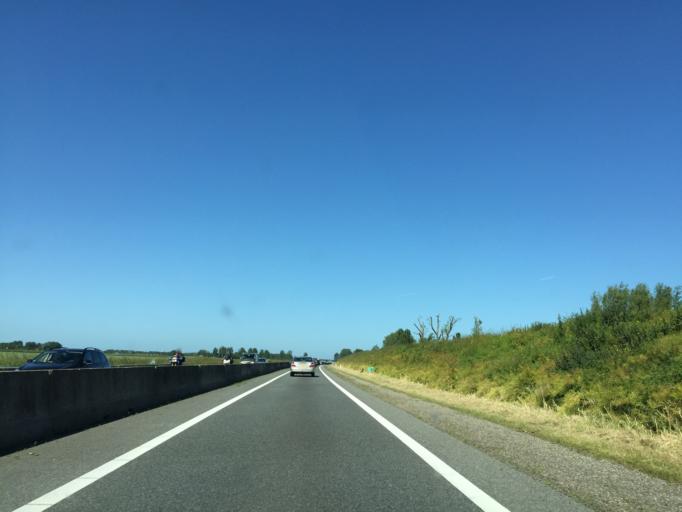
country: NL
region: South Holland
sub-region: Gemeente Hellevoetsluis
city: Nieuwenhoorn
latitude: 51.8581
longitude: 4.1368
